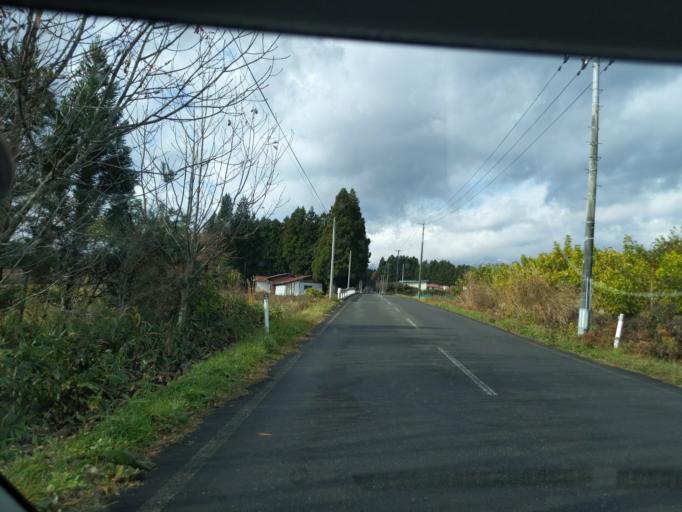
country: JP
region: Iwate
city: Mizusawa
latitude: 39.0983
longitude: 141.0026
